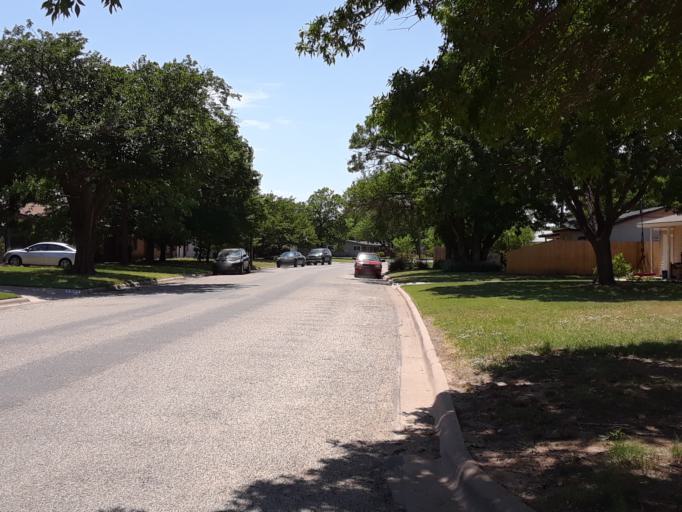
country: US
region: Texas
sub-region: Taylor County
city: Abilene
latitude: 32.4109
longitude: -99.7496
